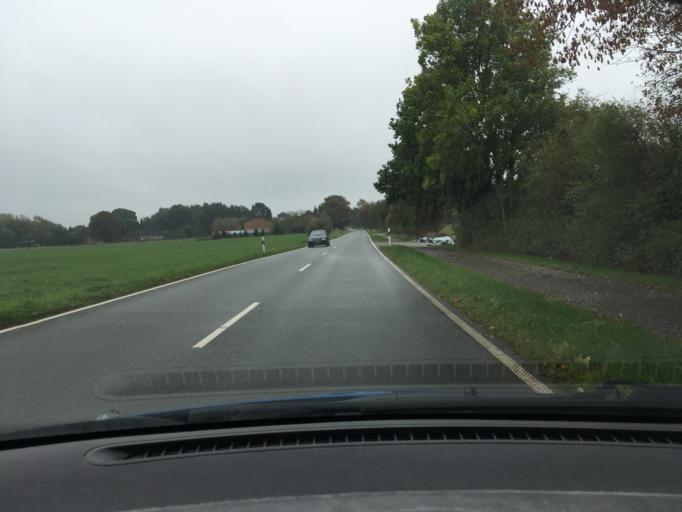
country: DE
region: Schleswig-Holstein
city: Bosdorf
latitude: 54.1139
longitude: 10.4776
